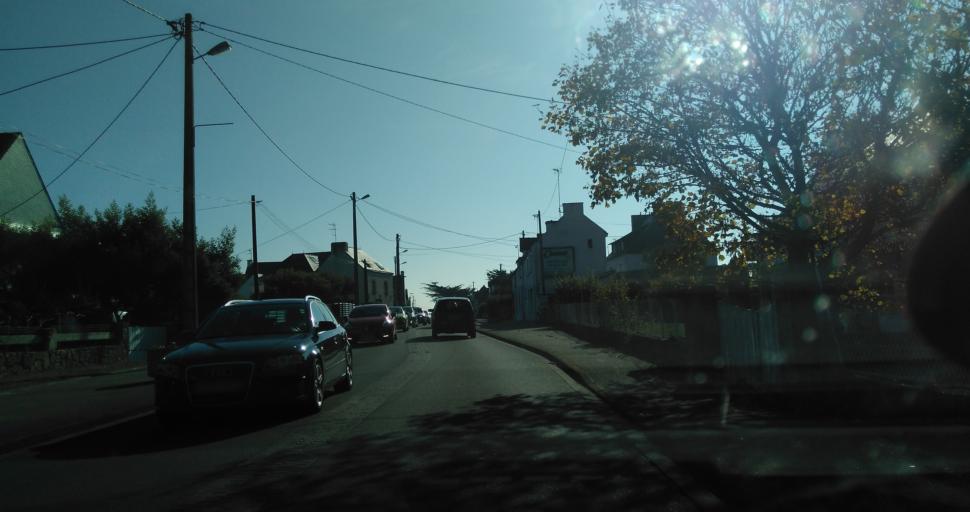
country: FR
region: Brittany
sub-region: Departement du Morbihan
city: Saint-Pierre-Quiberon
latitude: 47.5381
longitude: -3.1351
